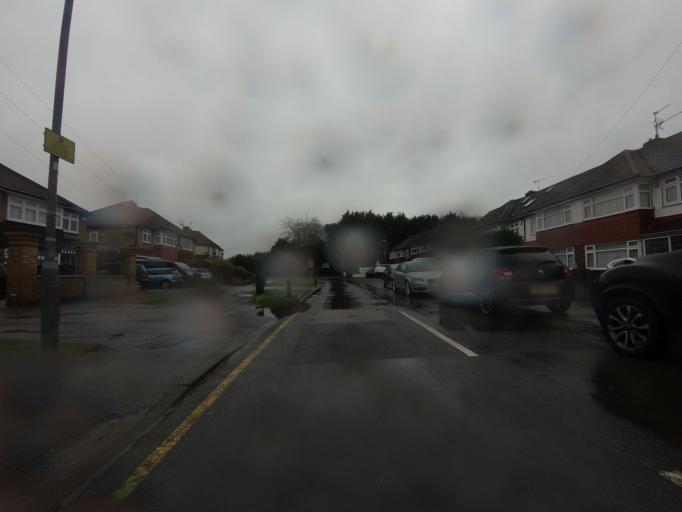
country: GB
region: England
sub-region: Hertfordshire
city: Cheshunt
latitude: 51.7141
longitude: -0.0511
